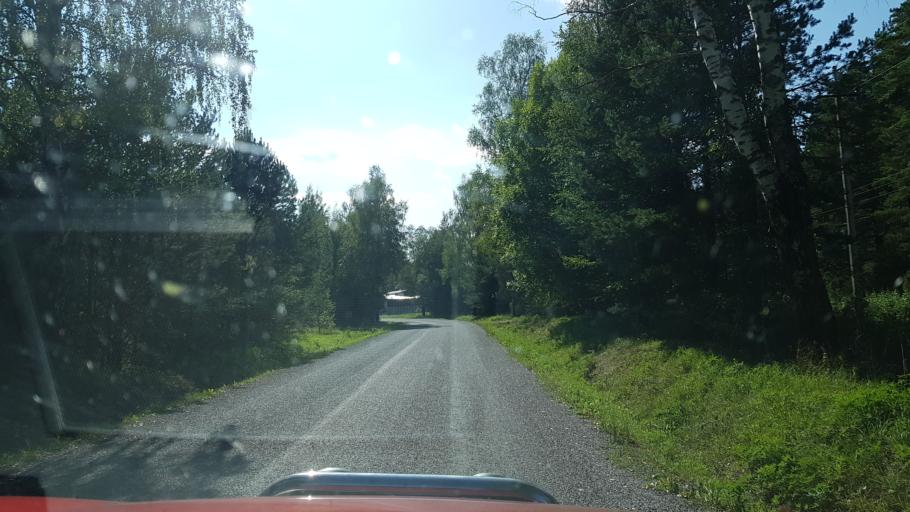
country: RU
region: Pskov
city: Pechory
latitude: 57.9577
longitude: 27.6148
